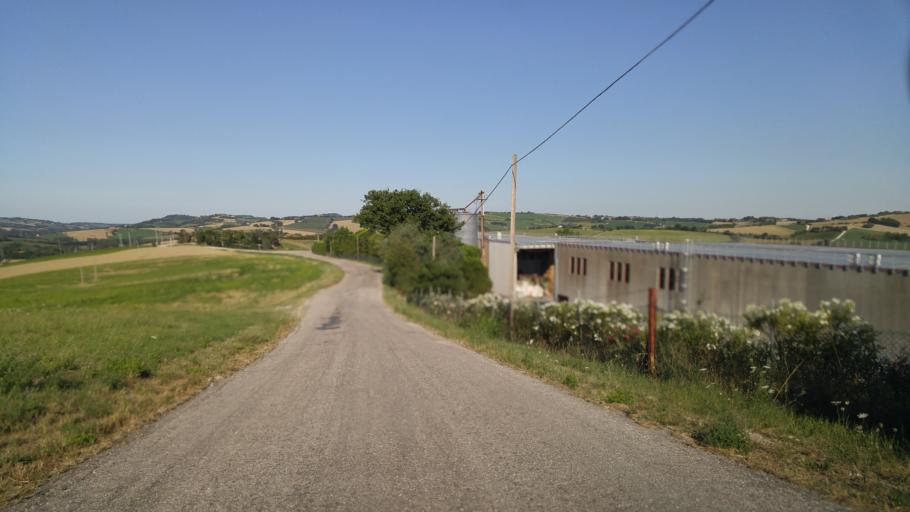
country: IT
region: The Marches
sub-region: Provincia di Pesaro e Urbino
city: Mombaroccio
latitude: 43.8119
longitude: 12.8675
